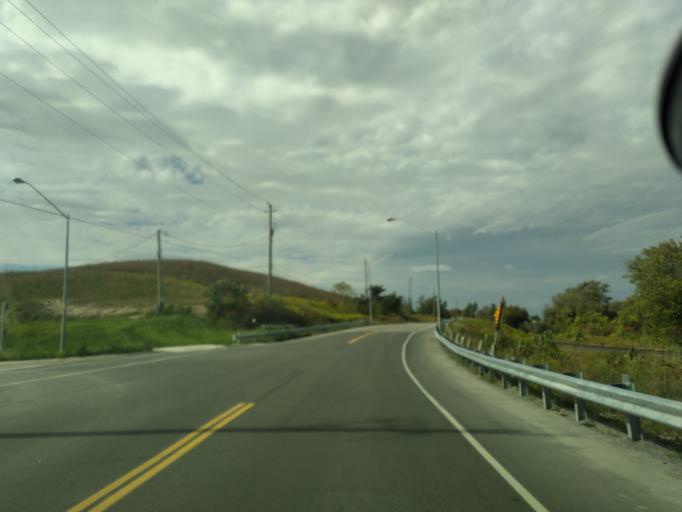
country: CA
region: Ontario
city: Newmarket
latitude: 44.0942
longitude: -79.4930
